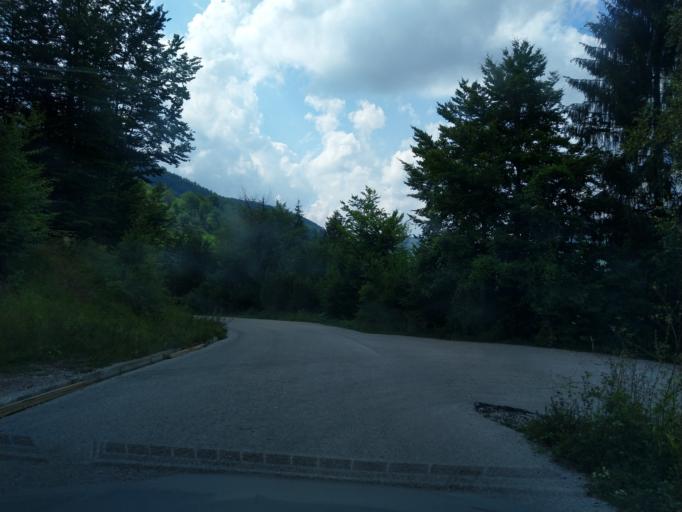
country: RS
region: Central Serbia
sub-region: Zlatiborski Okrug
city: Nova Varos
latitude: 43.5797
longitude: 19.8855
